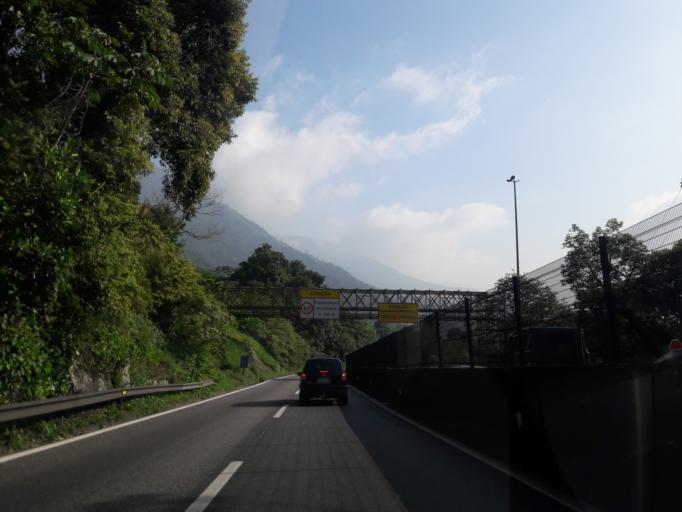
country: BR
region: Sao Paulo
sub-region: Cubatao
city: Cubatao
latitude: -23.8852
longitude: -46.4614
